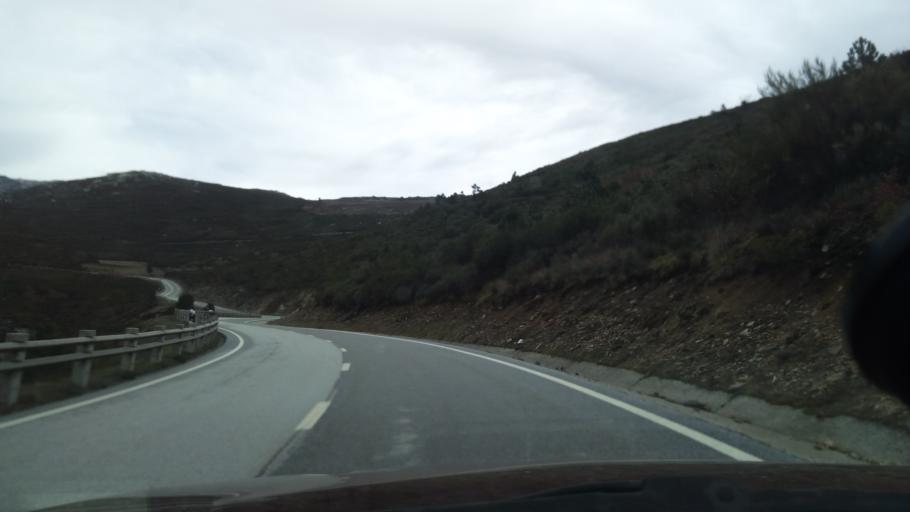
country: PT
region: Guarda
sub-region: Seia
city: Seia
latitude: 40.3487
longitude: -7.7113
